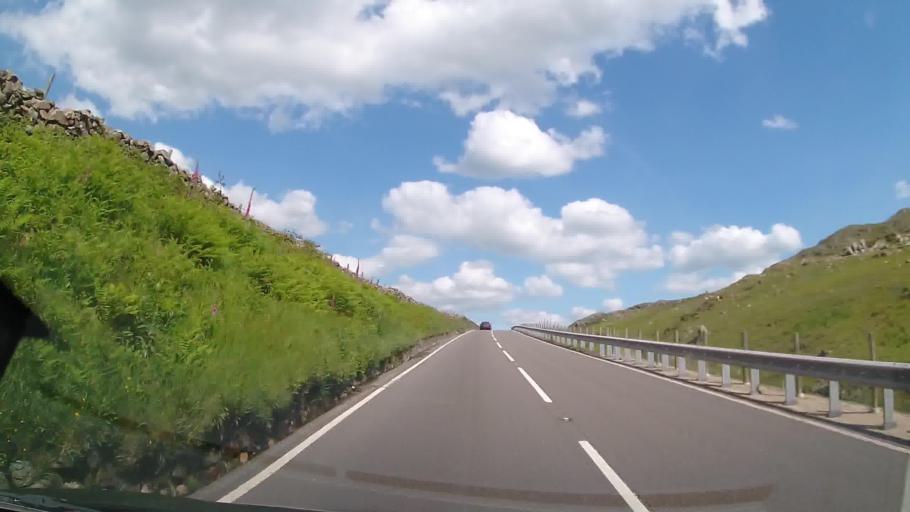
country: GB
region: Wales
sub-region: Gwynedd
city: Dolgellau
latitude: 52.7400
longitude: -3.7898
